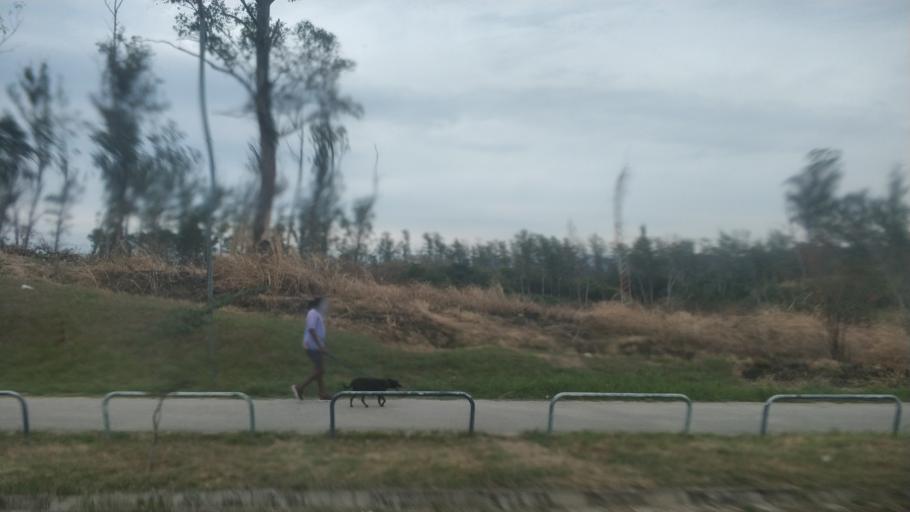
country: BR
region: Rio de Janeiro
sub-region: Seropedica
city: Seropedica
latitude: -22.7518
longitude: -43.6954
